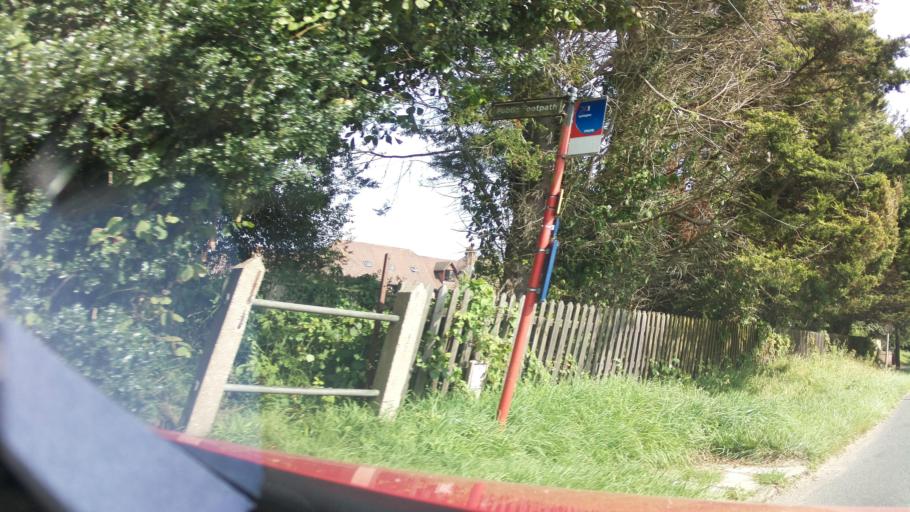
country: GB
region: England
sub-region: Hampshire
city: New Milton
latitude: 50.7430
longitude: -1.6471
